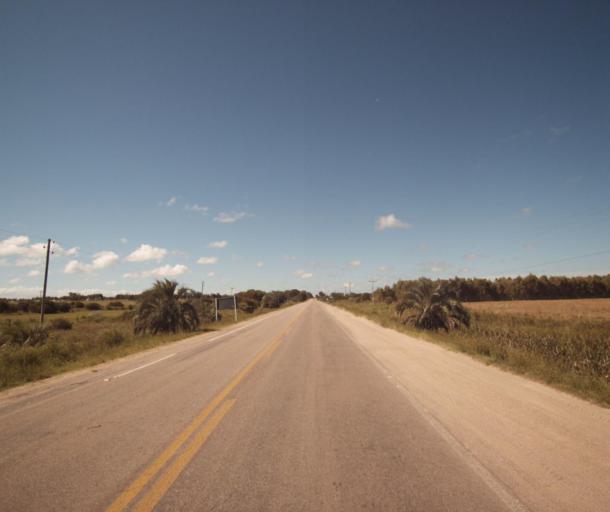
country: BR
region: Rio Grande do Sul
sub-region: Chui
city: Chui
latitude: -33.6701
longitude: -53.4417
